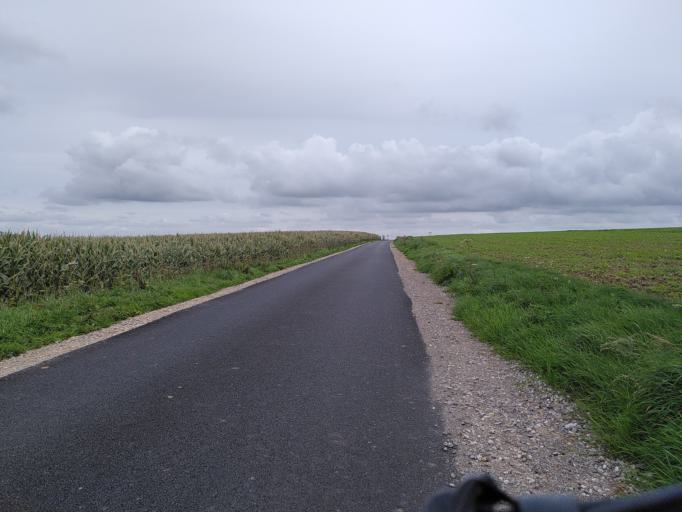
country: FR
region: Nord-Pas-de-Calais
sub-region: Departement du Pas-de-Calais
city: Desvres
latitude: 50.6480
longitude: 1.9570
